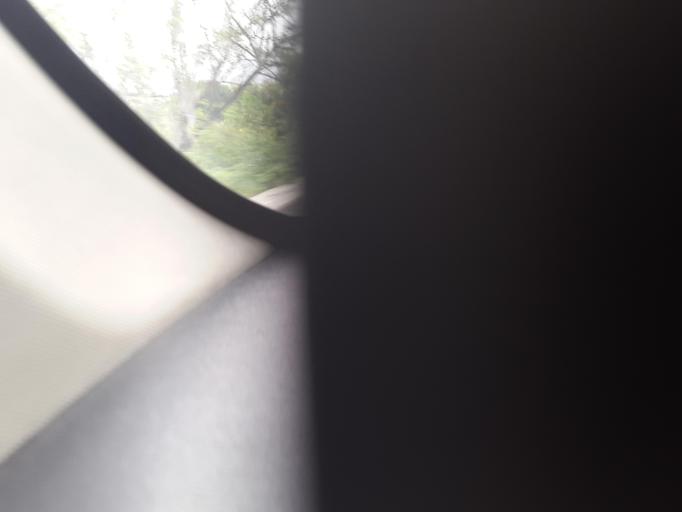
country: ID
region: West Java
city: Bandung
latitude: -6.8812
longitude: 107.6490
